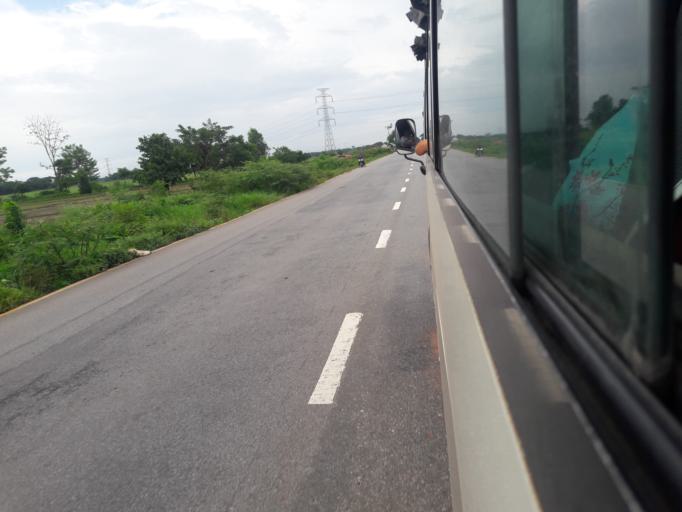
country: MM
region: Bago
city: Nyaunglebin
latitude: 17.8412
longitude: 96.6853
